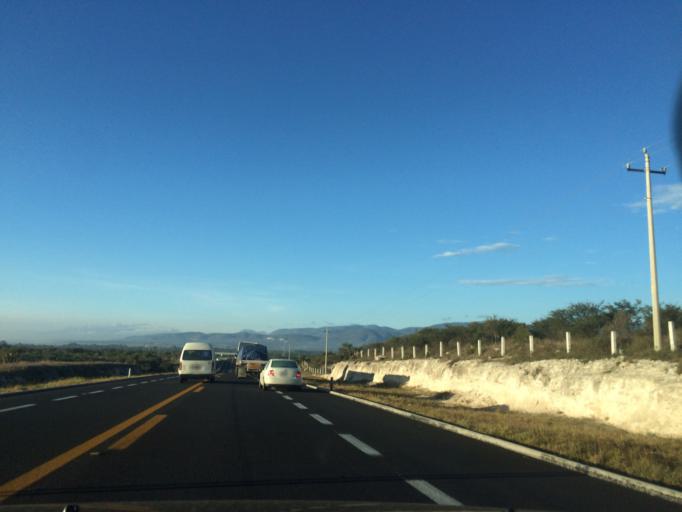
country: MX
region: Puebla
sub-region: Tehuacan
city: Magdalena Cuayucatepec
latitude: 18.5574
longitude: -97.4632
